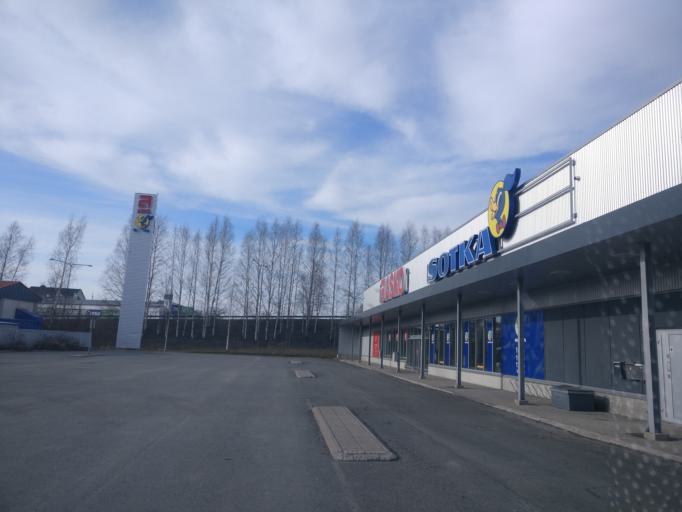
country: FI
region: Lapland
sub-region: Kemi-Tornio
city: Kemi
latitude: 65.7397
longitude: 24.5684
